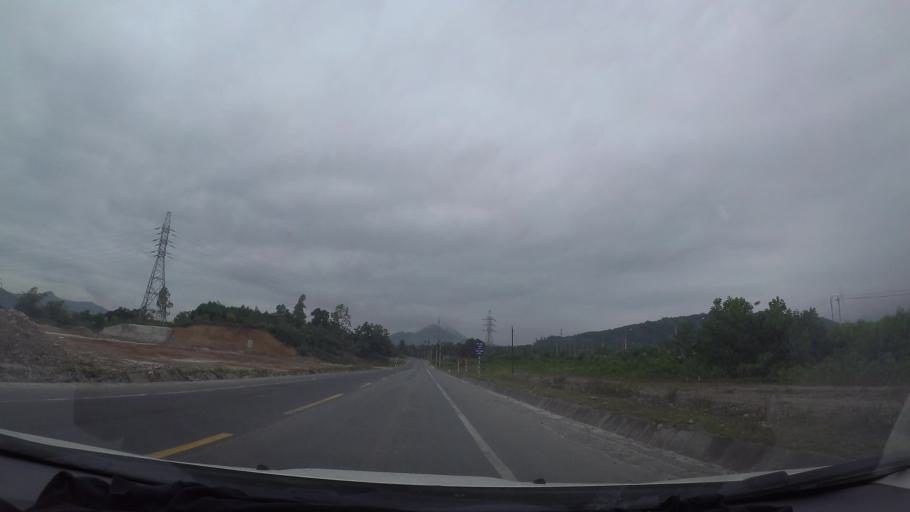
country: VN
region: Da Nang
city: Lien Chieu
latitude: 16.0836
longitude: 108.0847
